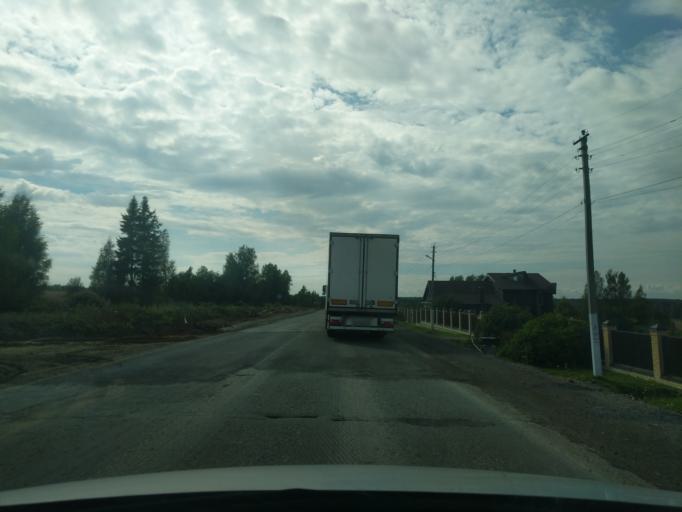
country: RU
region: Kostroma
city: Sudislavl'
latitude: 57.8608
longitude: 41.6164
